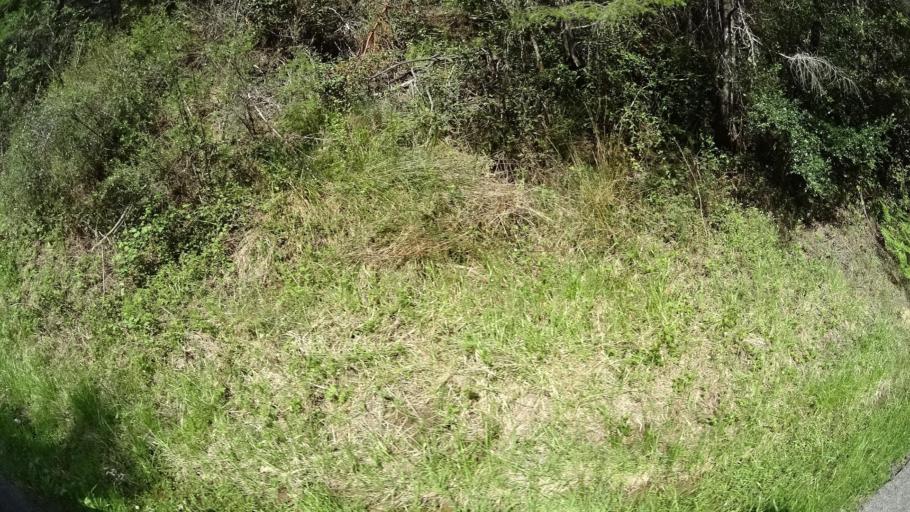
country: US
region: California
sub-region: Humboldt County
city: Redway
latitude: 40.4350
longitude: -123.7754
